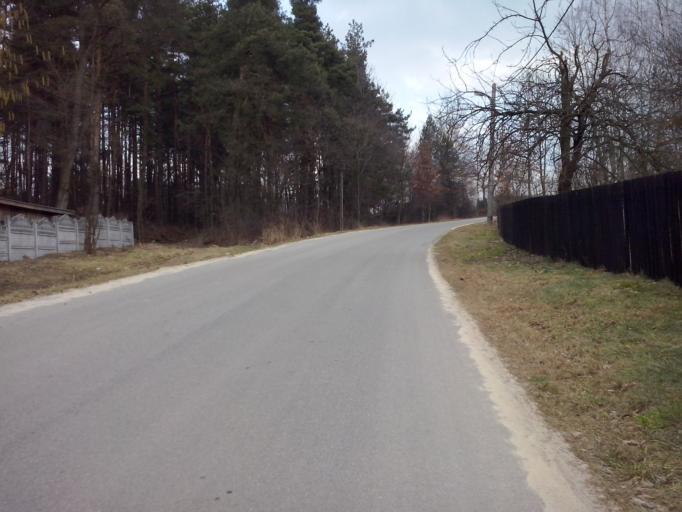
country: PL
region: Subcarpathian Voivodeship
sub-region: Powiat nizanski
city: Krzeszow
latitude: 50.4267
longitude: 22.3374
